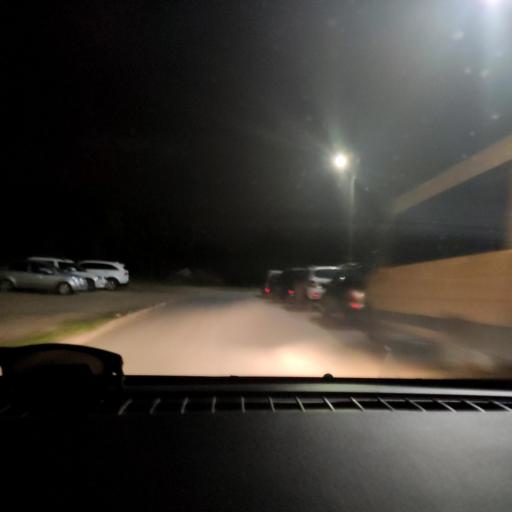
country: RU
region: Samara
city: Novokuybyshevsk
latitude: 53.1028
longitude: 49.9740
